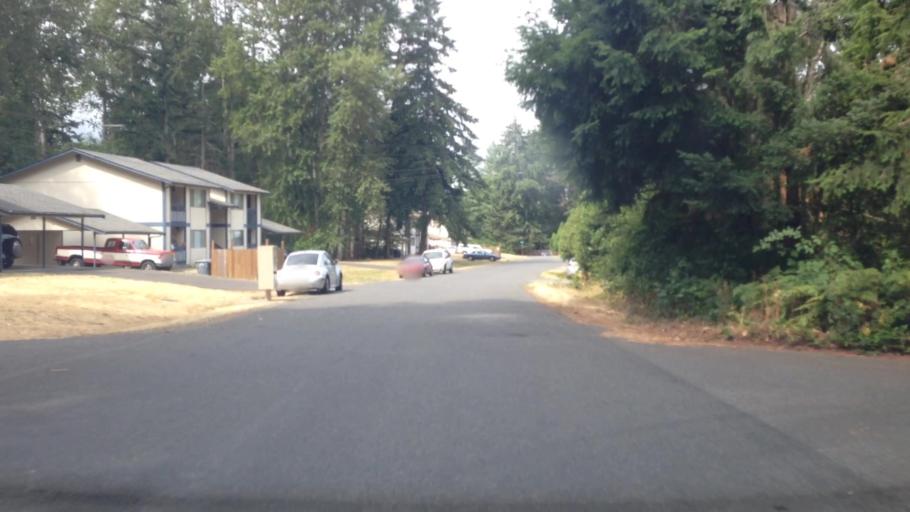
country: US
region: Washington
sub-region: Pierce County
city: South Hill
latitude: 47.1127
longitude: -122.2961
